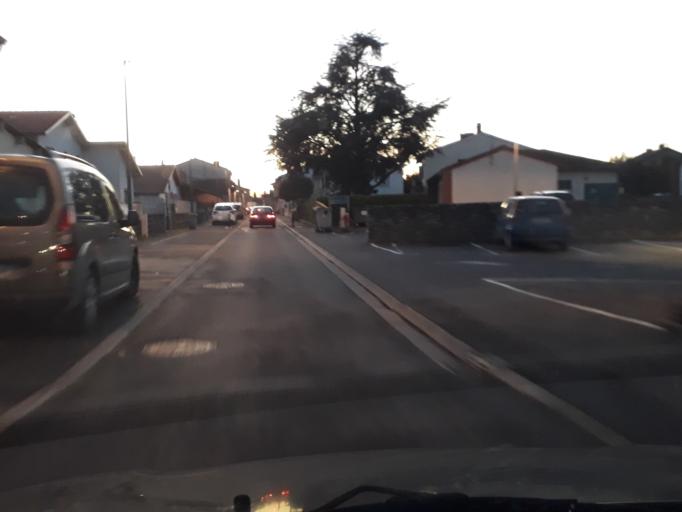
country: FR
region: Midi-Pyrenees
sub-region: Departement de la Haute-Garonne
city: Carbonne
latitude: 43.2970
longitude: 1.2213
